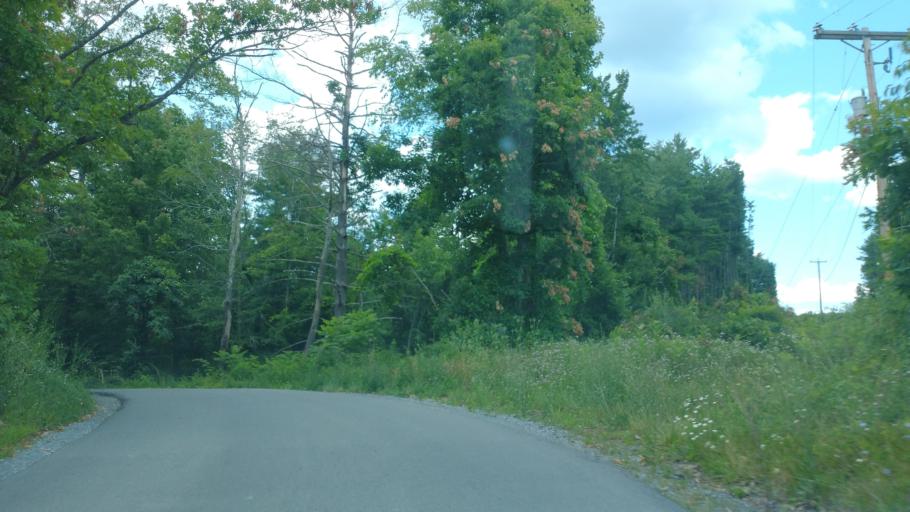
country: US
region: West Virginia
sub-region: Mercer County
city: Athens
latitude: 37.4508
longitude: -81.0620
